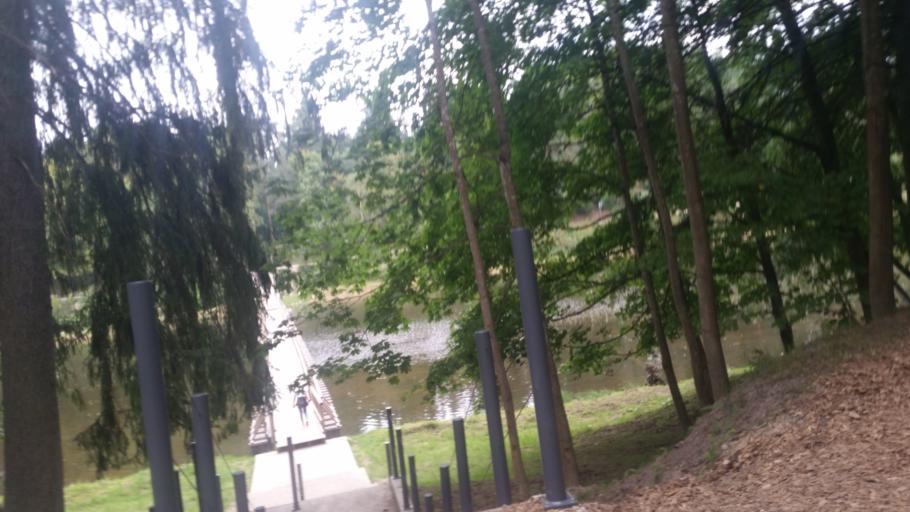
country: LV
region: Ogre
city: Ogre
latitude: 56.8153
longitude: 24.6148
